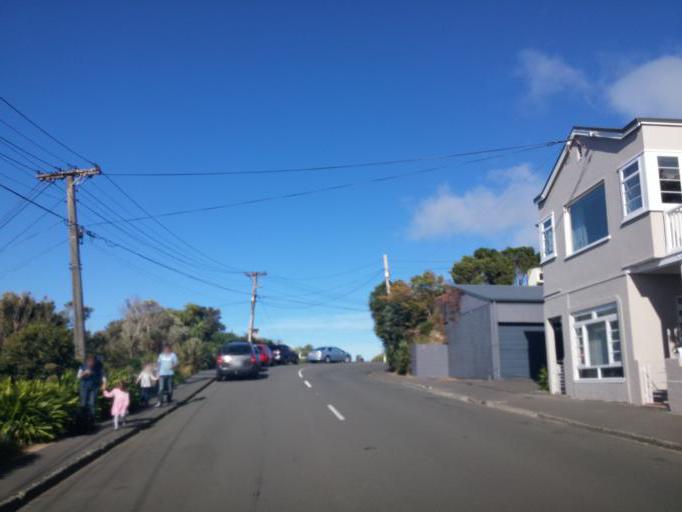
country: NZ
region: Wellington
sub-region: Wellington City
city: Kelburn
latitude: -41.2884
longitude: 174.7503
